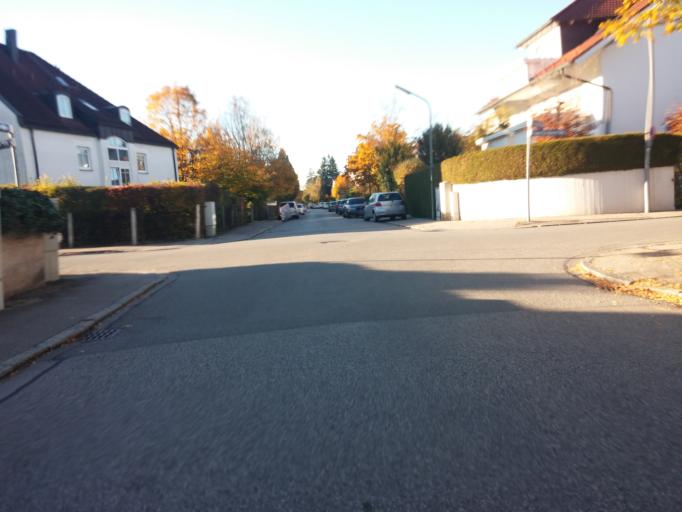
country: DE
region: Bavaria
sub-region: Upper Bavaria
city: Haar
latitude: 48.1084
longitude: 11.7078
